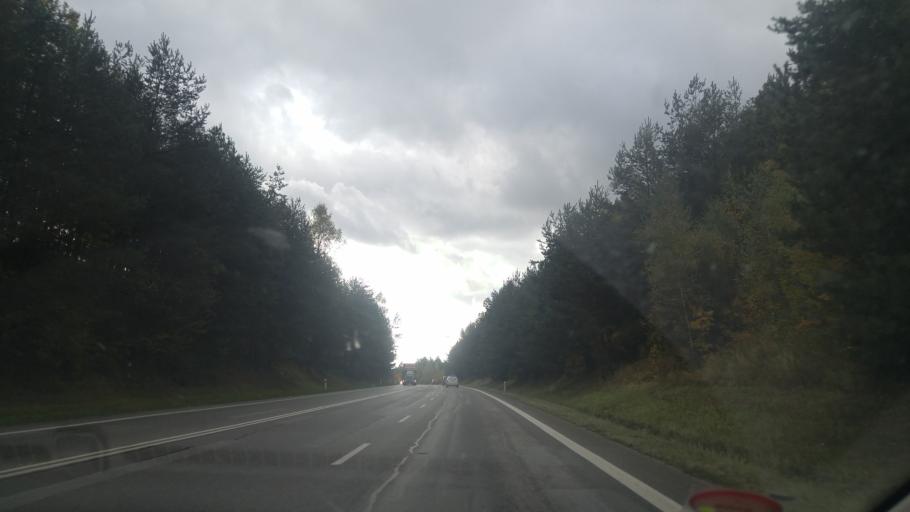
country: CZ
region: Jihocesky
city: Sevetin
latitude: 49.1051
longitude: 14.5628
